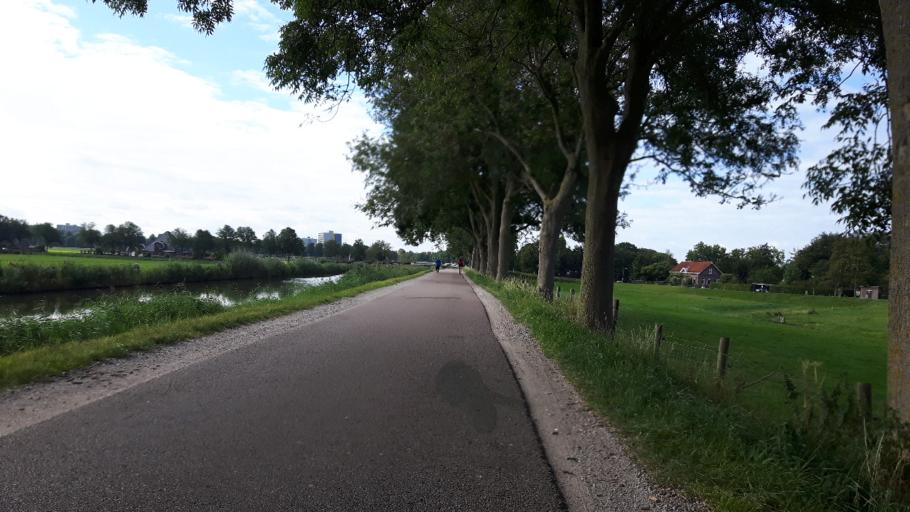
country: NL
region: North Holland
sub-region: Gemeente Purmerend
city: Purmerend
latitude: 52.5361
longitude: 4.9614
